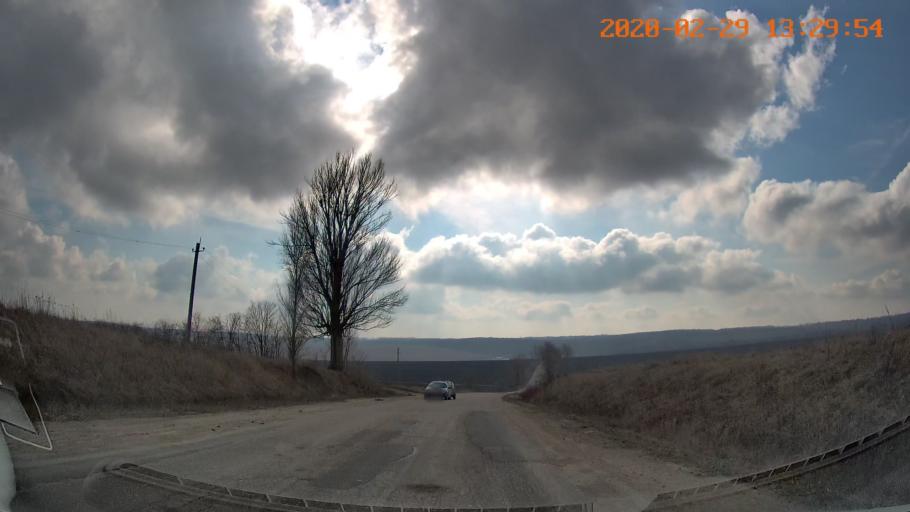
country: MD
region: Telenesti
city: Camenca
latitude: 47.8922
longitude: 28.6330
